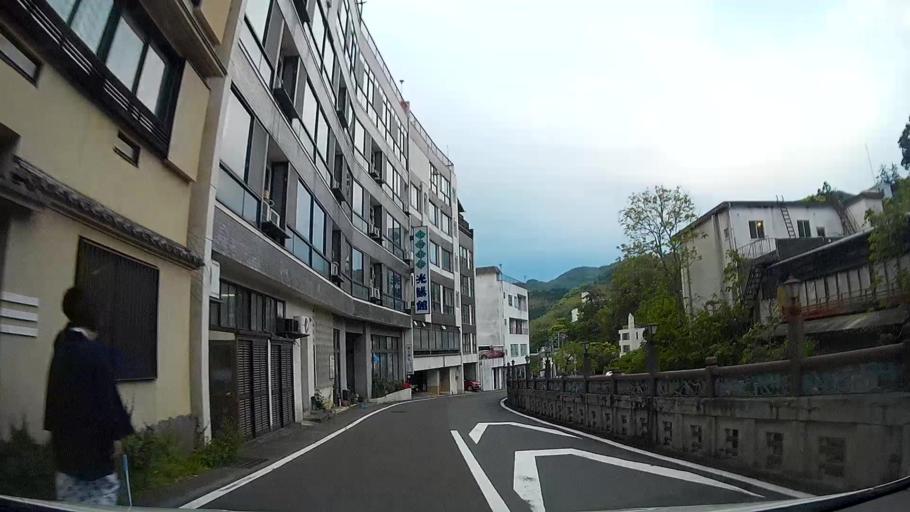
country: JP
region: Kanagawa
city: Yugawara
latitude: 35.1477
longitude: 139.0721
